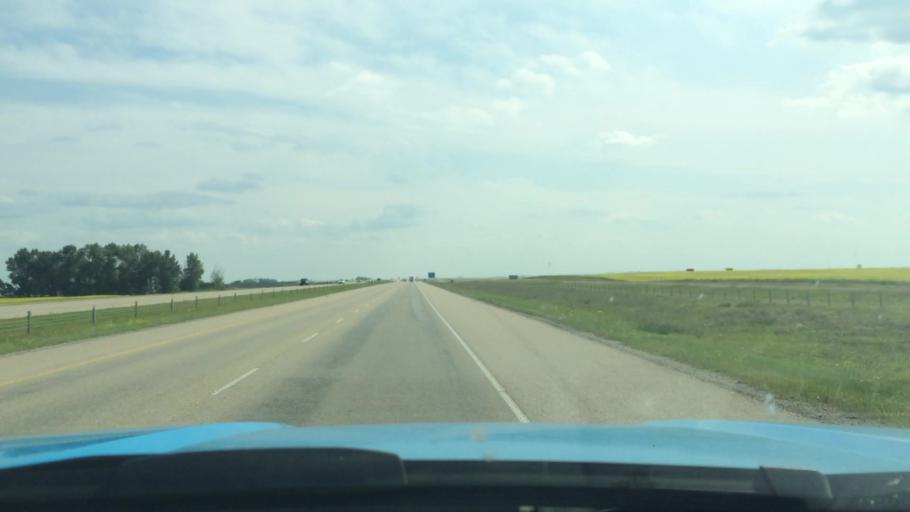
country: CA
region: Alberta
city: Carstairs
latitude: 51.5870
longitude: -114.0253
